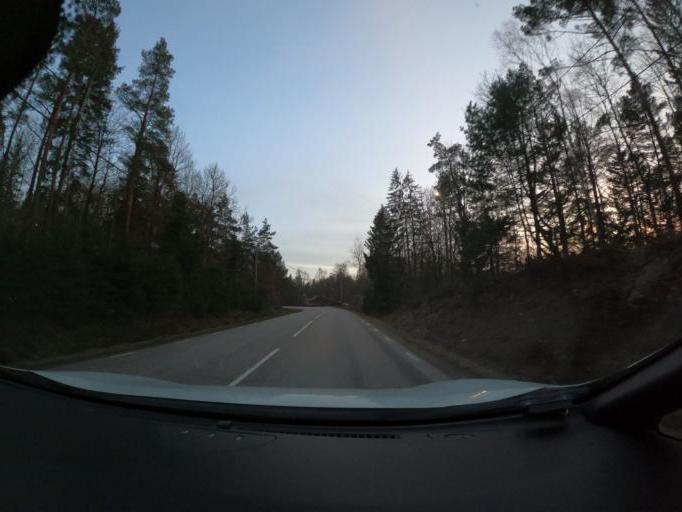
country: SE
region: Vaestra Goetaland
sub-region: Harryda Kommun
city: Landvetter
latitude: 57.6333
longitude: 12.1786
